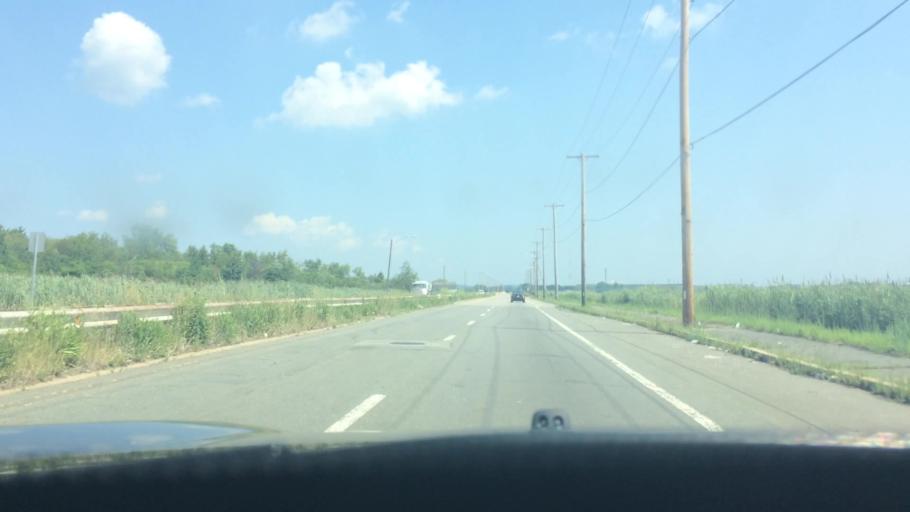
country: US
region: Massachusetts
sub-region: Suffolk County
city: Revere
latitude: 42.4240
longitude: -71.0025
